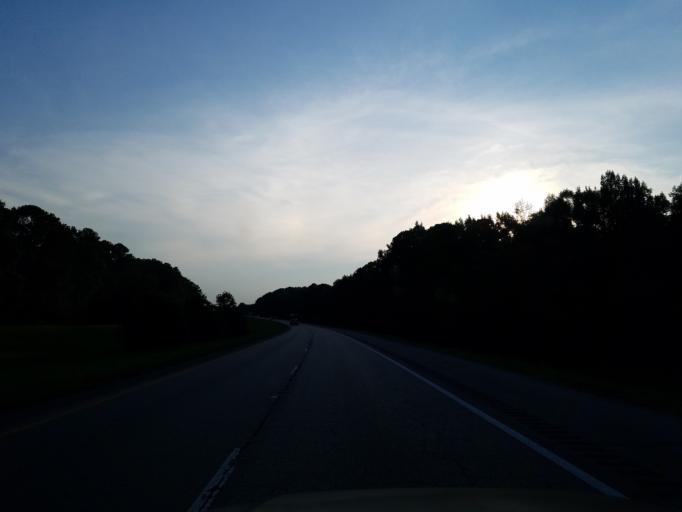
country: US
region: Mississippi
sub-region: Lauderdale County
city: Marion
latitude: 32.4136
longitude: -88.5212
